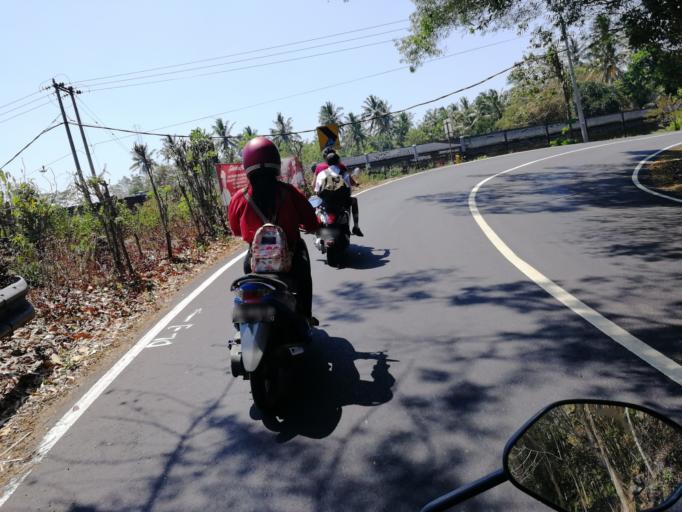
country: ID
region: Bali
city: Abang
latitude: -8.3926
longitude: 115.5981
